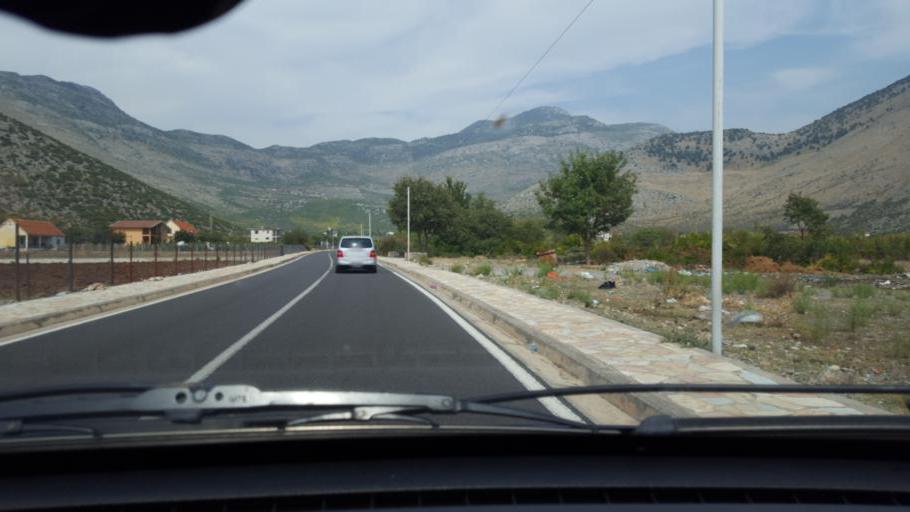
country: AL
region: Shkoder
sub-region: Rrethi i Malesia e Madhe
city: Hot
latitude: 42.3470
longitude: 19.4402
